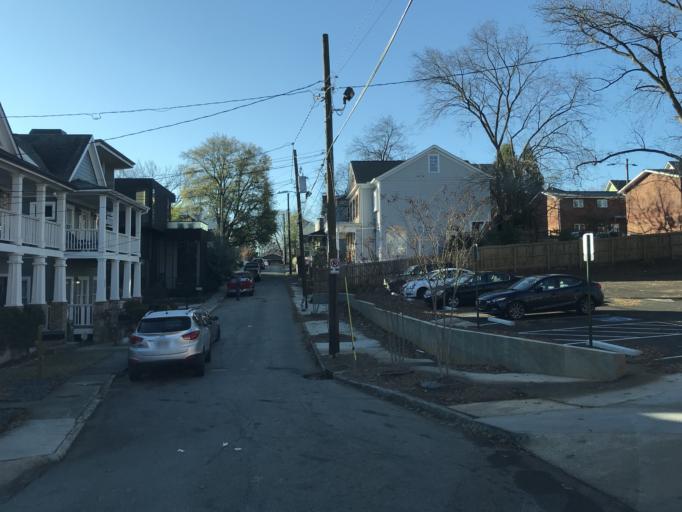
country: US
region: Georgia
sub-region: Fulton County
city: Atlanta
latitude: 33.7608
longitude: -84.3663
